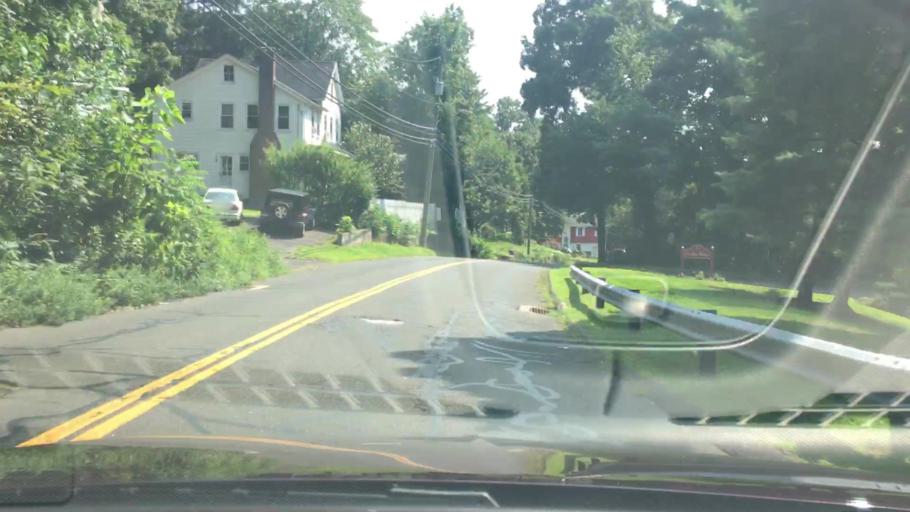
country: US
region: Connecticut
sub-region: Fairfield County
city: Norwalk
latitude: 41.1389
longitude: -73.4222
